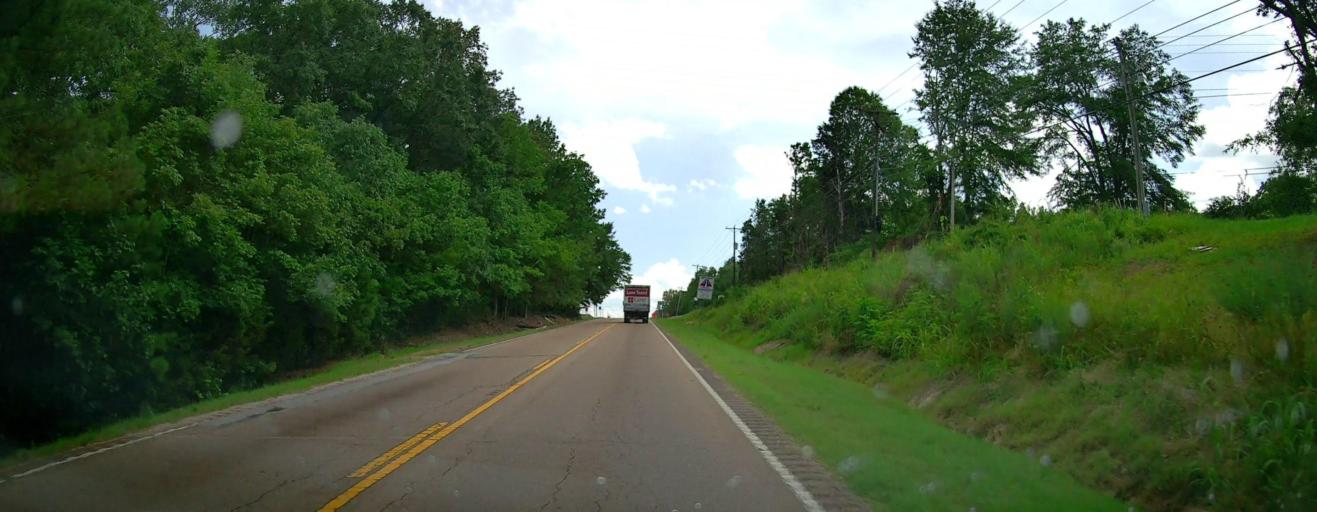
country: US
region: Mississippi
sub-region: Lee County
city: Shannon
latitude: 34.1331
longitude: -88.7194
